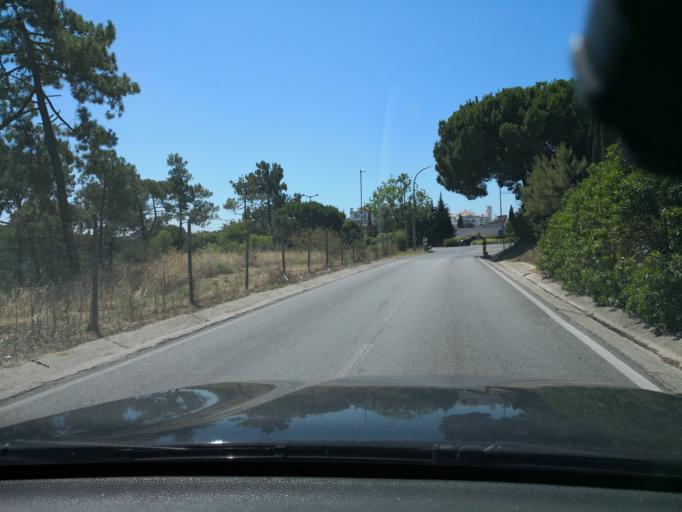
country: PT
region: Faro
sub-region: Loule
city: Quarteira
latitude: 37.0782
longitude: -8.0978
